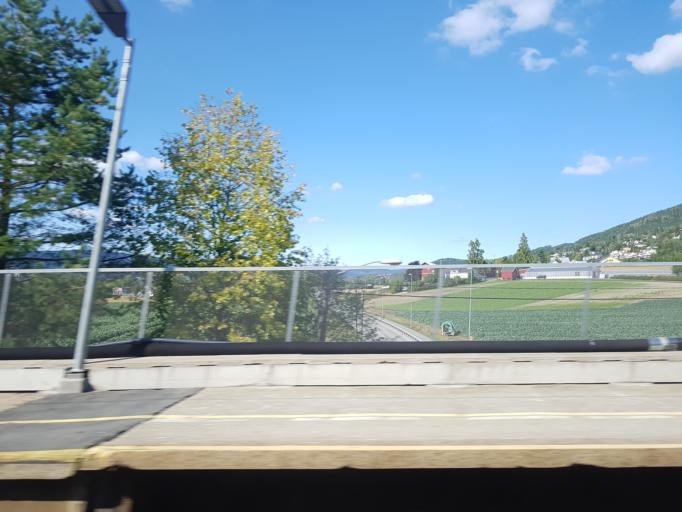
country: NO
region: Buskerud
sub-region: Lier
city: Lierbyen
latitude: 59.7630
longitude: 10.2888
